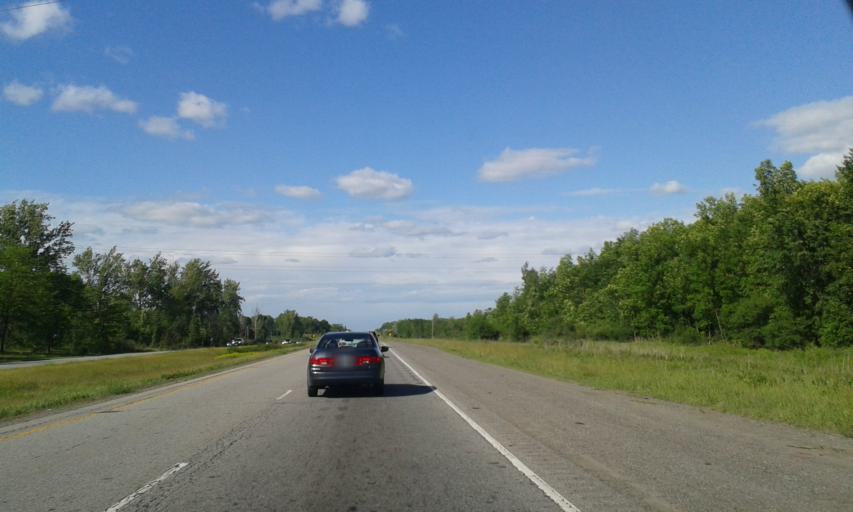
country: CA
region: Ontario
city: Brockville
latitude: 44.6651
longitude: -75.6113
